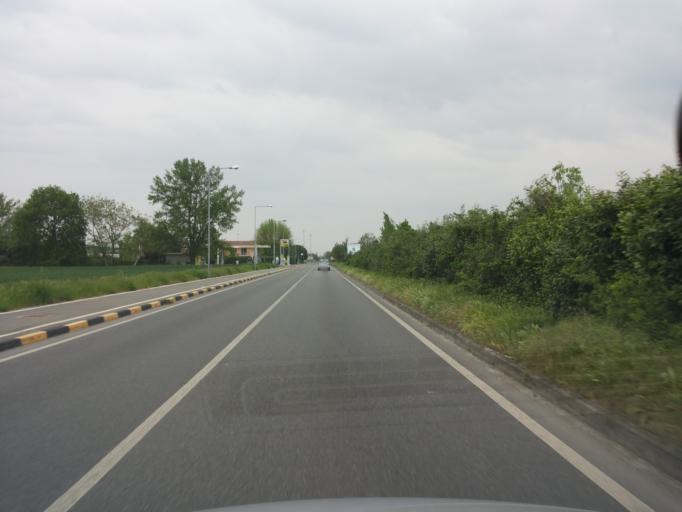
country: IT
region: Piedmont
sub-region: Provincia di Alessandria
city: Casale Monferrato
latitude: 45.1098
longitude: 8.4518
